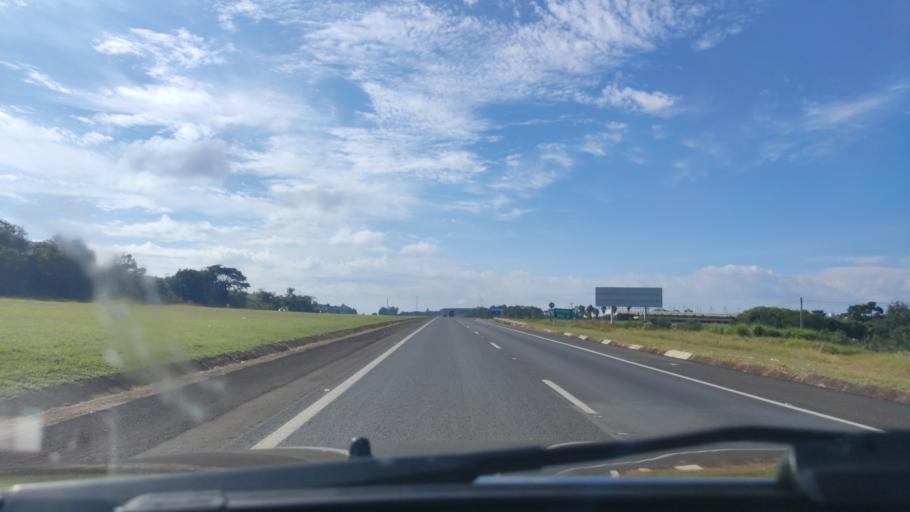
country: BR
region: Sao Paulo
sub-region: Itatinga
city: Itatinga
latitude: -23.1547
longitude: -48.3819
